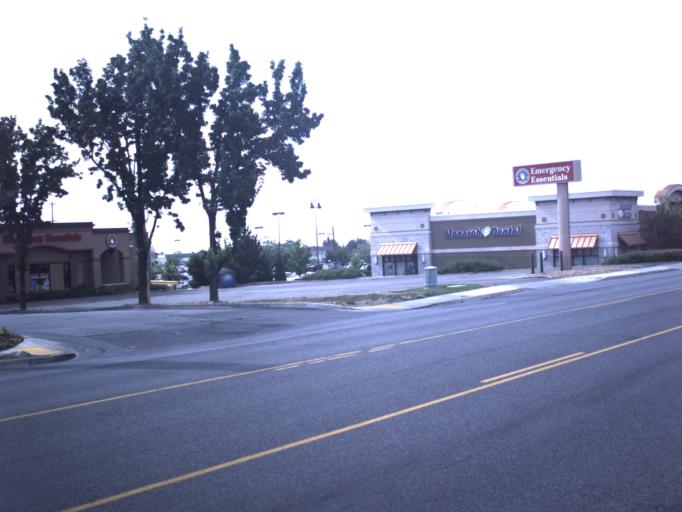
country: US
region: Utah
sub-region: Davis County
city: West Bountiful
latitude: 40.8883
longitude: -111.8921
